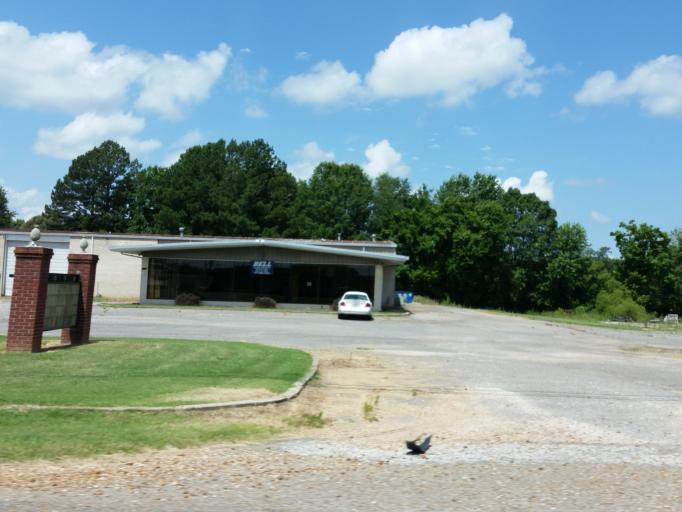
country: US
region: Tennessee
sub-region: Weakley County
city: Martin
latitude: 36.3624
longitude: -88.8499
